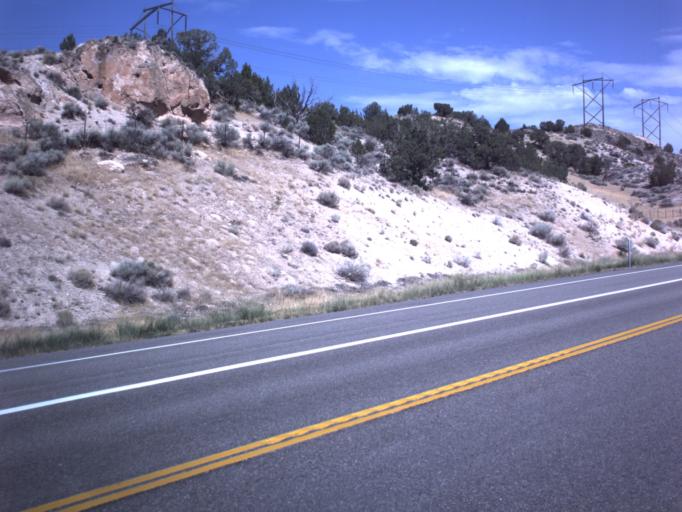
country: US
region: Utah
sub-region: Sanpete County
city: Gunnison
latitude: 39.3555
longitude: -111.9296
